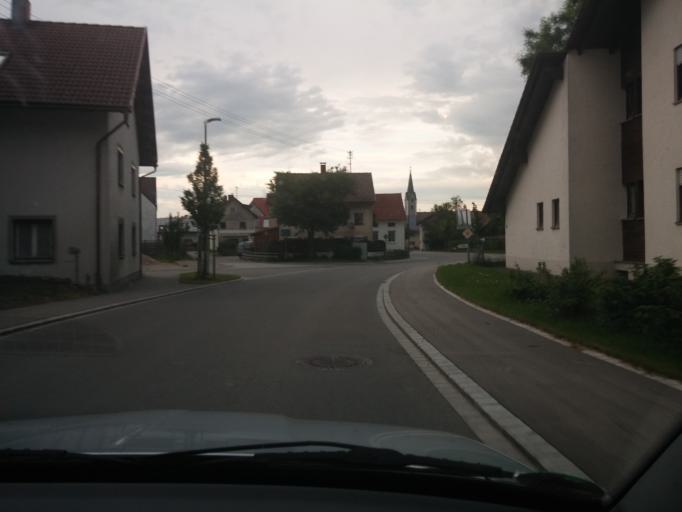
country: DE
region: Bavaria
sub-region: Swabia
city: Legau
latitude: 47.8537
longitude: 10.1280
